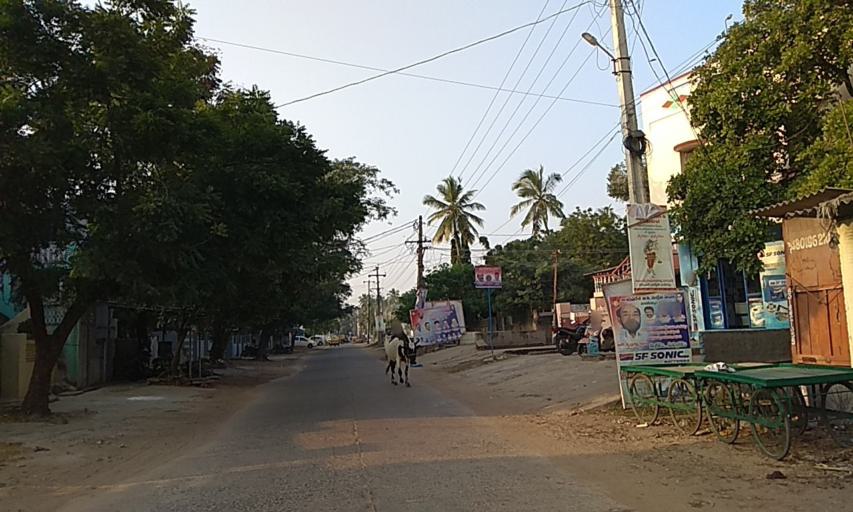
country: IN
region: Andhra Pradesh
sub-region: Krishna
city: Machilipatnam
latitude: 16.1866
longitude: 81.1350
